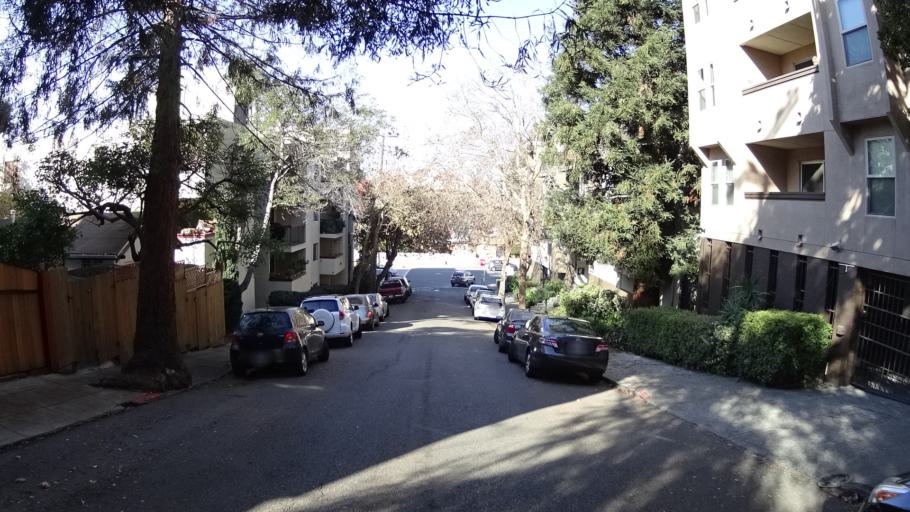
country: US
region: California
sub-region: Alameda County
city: Oakland
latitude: 37.8171
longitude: -122.2550
